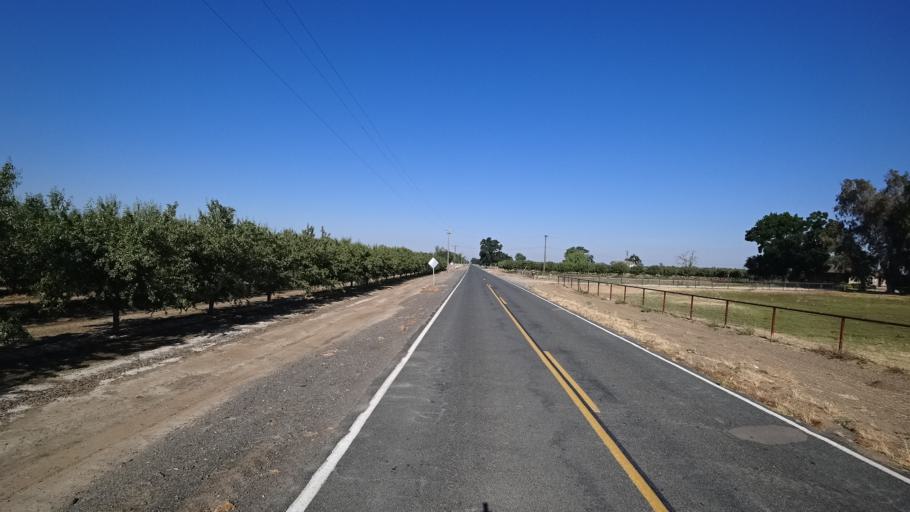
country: US
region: California
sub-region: Fresno County
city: Riverdale
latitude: 36.3658
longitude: -119.8280
